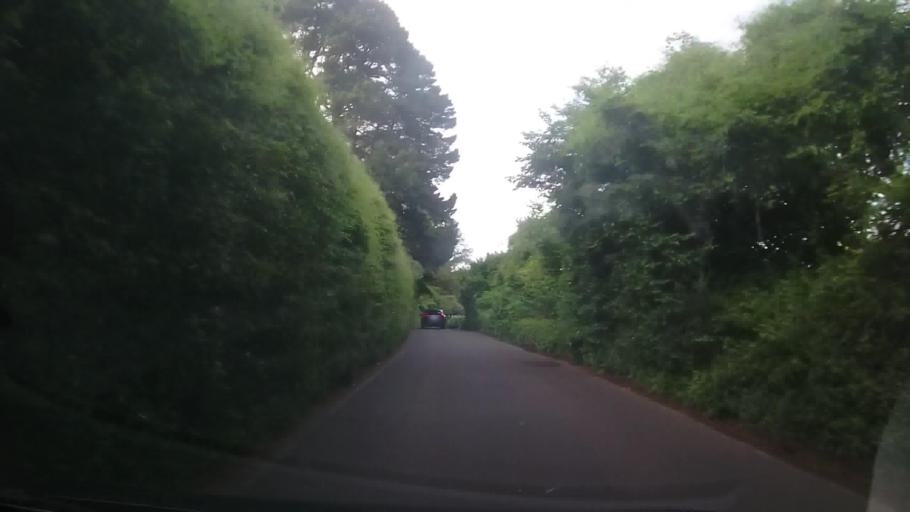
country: GB
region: England
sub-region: Devon
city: Kingsbridge
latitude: 50.2743
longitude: -3.7637
